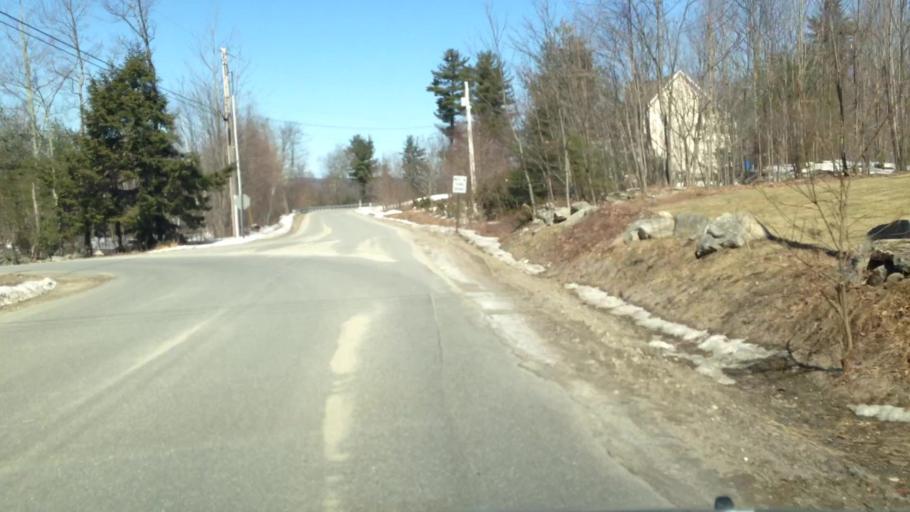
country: US
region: New Hampshire
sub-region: Hillsborough County
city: New Boston
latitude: 42.9946
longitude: -71.6498
